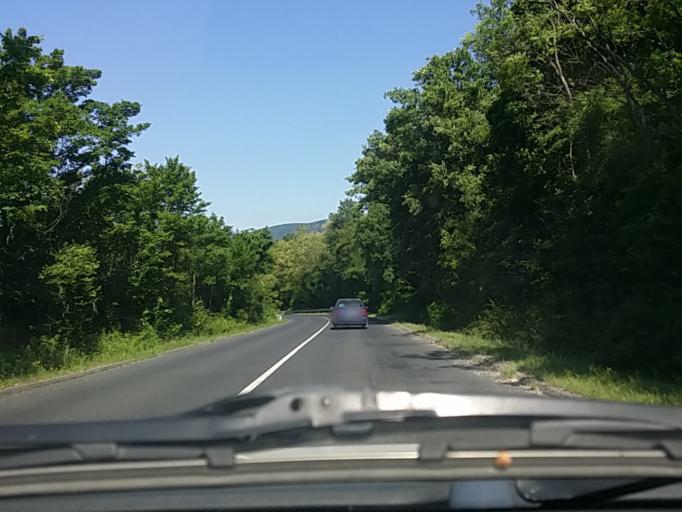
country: HU
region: Pest
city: Csobanka
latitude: 47.6678
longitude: 18.9569
